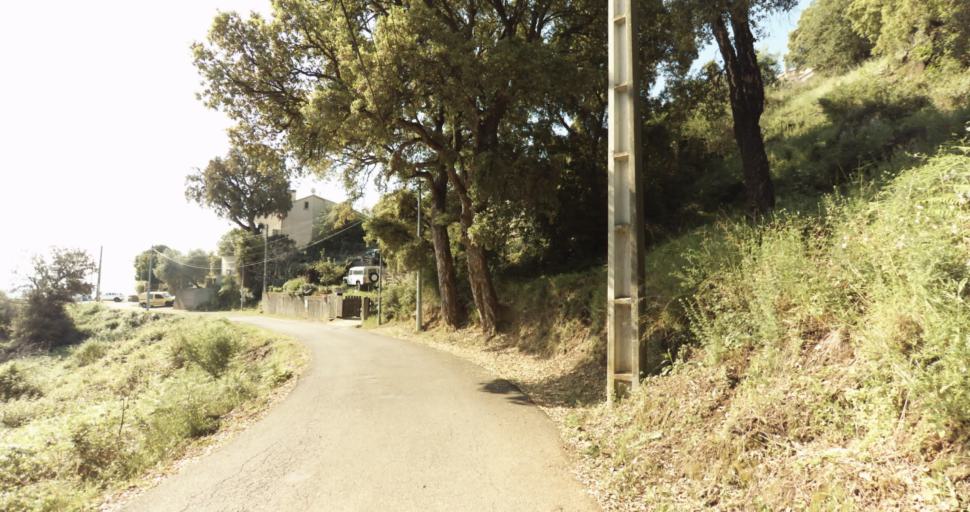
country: FR
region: Corsica
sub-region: Departement de la Haute-Corse
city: Biguglia
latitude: 42.6306
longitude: 9.4177
